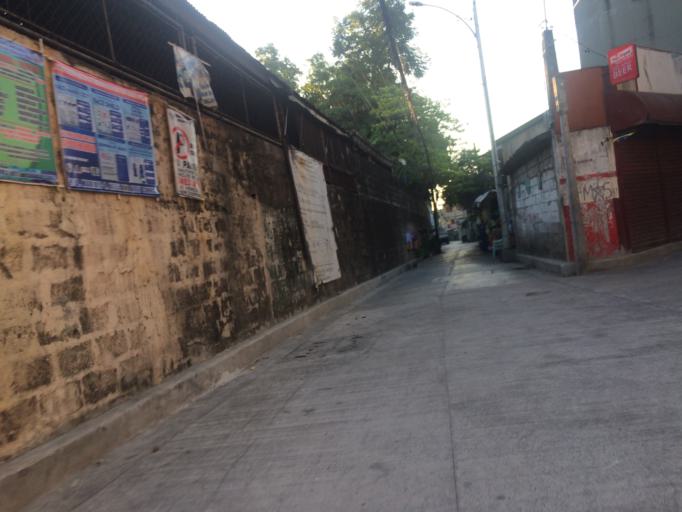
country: PH
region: Calabarzon
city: Bagong Pagasa
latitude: 14.6782
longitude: 121.0215
